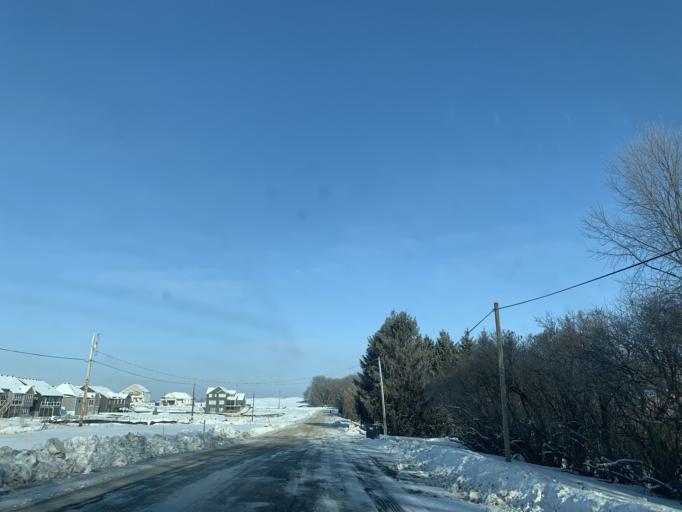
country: US
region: Minnesota
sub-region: Dakota County
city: Lakeville
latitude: 44.6569
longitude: -93.2275
